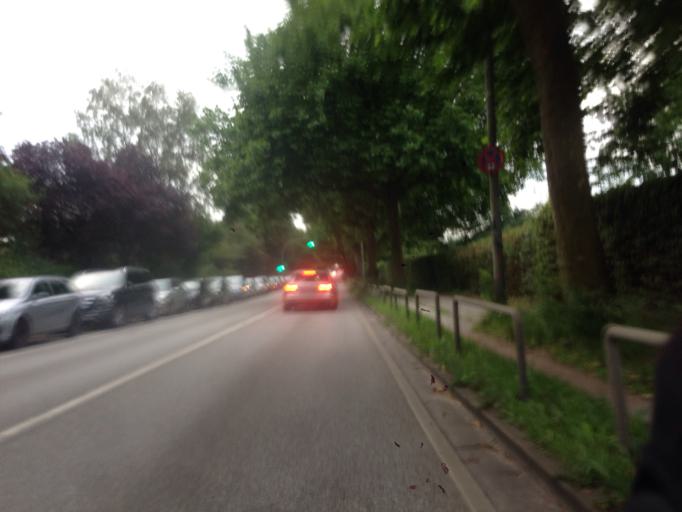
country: DE
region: Hamburg
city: Barmbek-Nord
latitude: 53.6059
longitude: 10.0344
